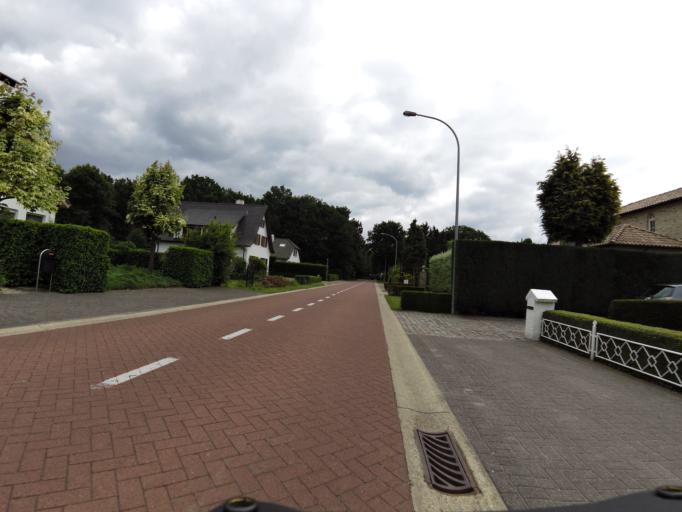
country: BE
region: Flanders
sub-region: Provincie Antwerpen
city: Hoogstraten
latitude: 51.4856
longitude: 4.7932
